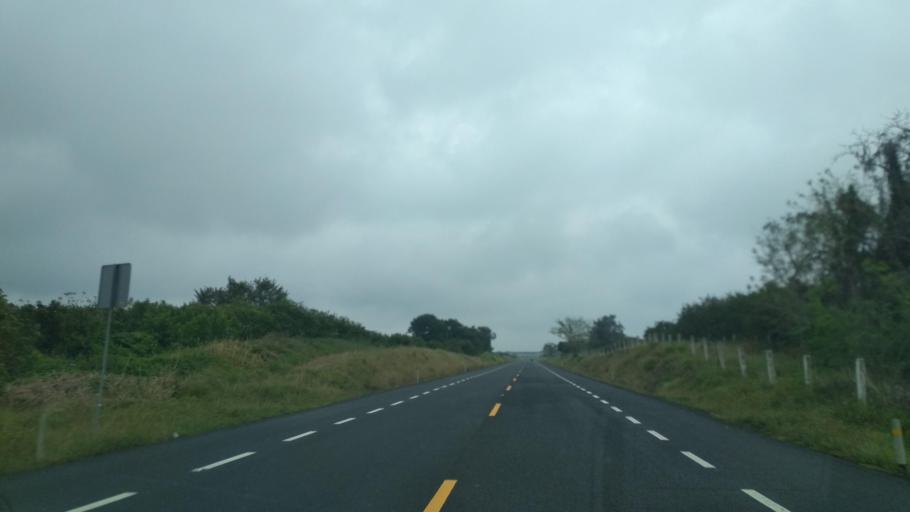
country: MX
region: Veracruz
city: Vega de San Marcos
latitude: 20.1972
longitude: -96.9744
